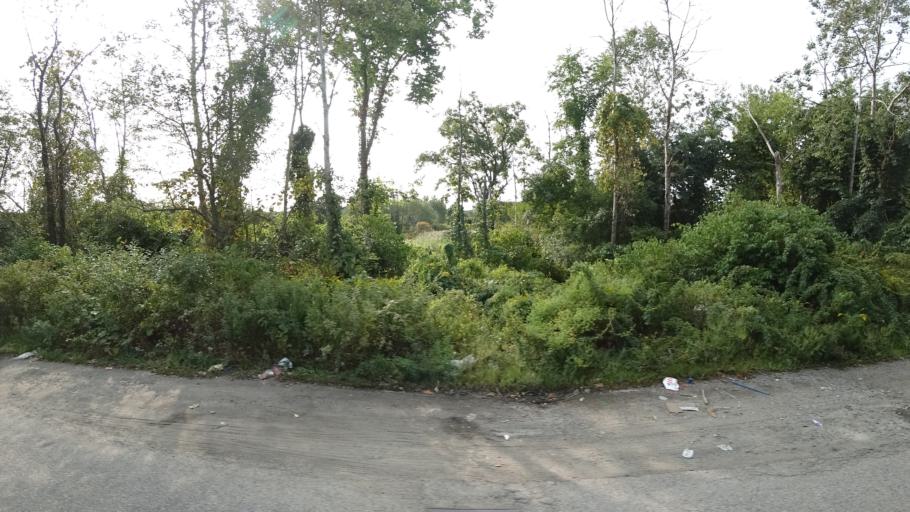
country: US
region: Massachusetts
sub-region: Norfolk County
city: Dedham
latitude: 42.2317
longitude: -71.1295
